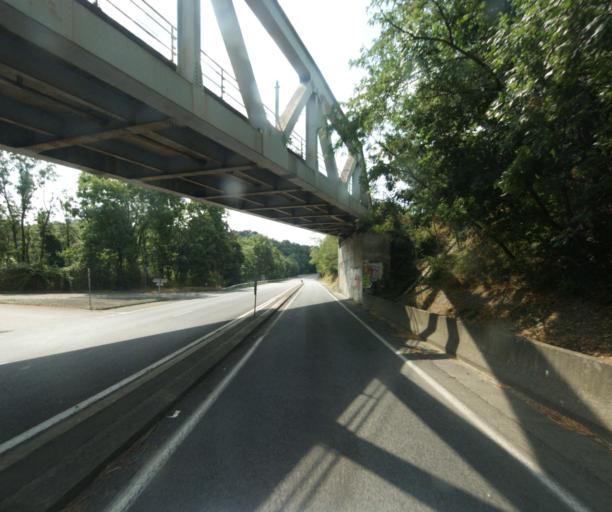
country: FR
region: Rhone-Alpes
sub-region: Departement du Rhone
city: Lentilly
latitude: 45.8339
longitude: 4.6624
